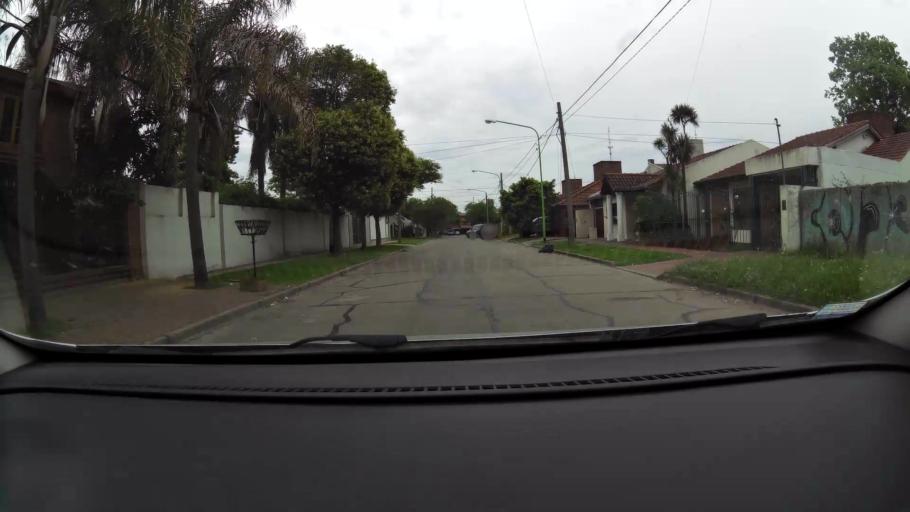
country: AR
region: Buenos Aires
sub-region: Partido de Campana
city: Campana
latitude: -34.1805
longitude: -58.9579
